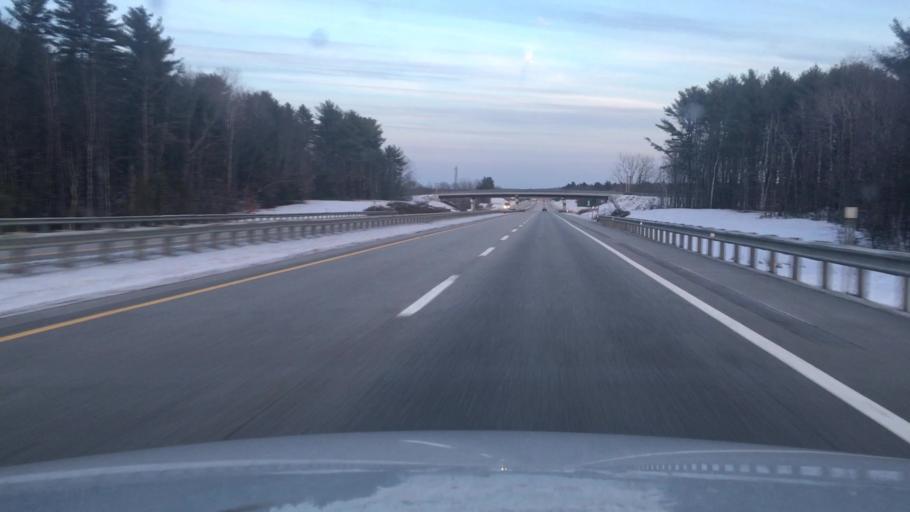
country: US
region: Maine
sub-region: Sagadahoc County
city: Richmond
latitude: 44.1431
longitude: -69.9282
